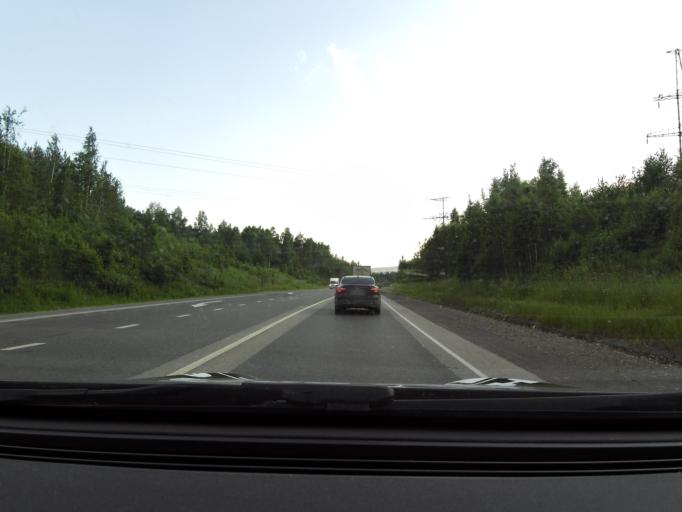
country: RU
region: Sverdlovsk
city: Talitsa
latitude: 56.8306
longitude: 59.9948
